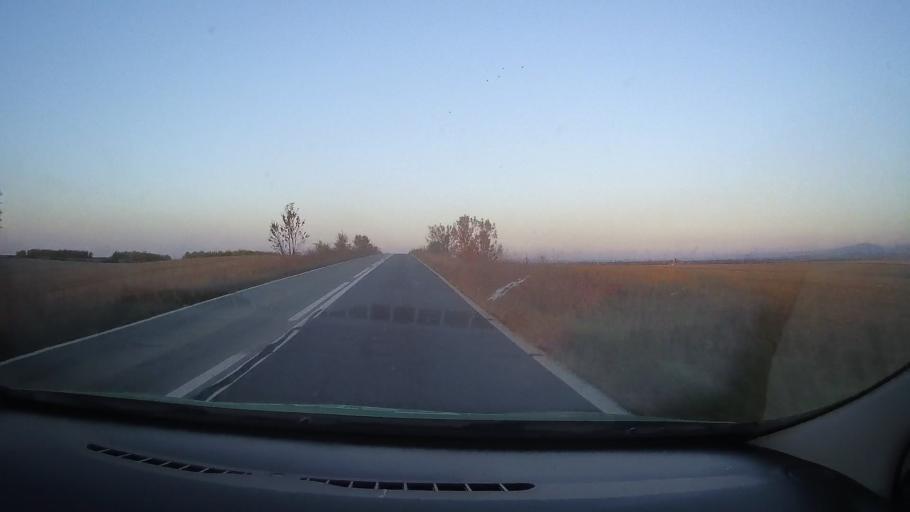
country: RO
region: Timis
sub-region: Comuna Manastiur
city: Manastiur
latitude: 45.8191
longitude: 22.0799
